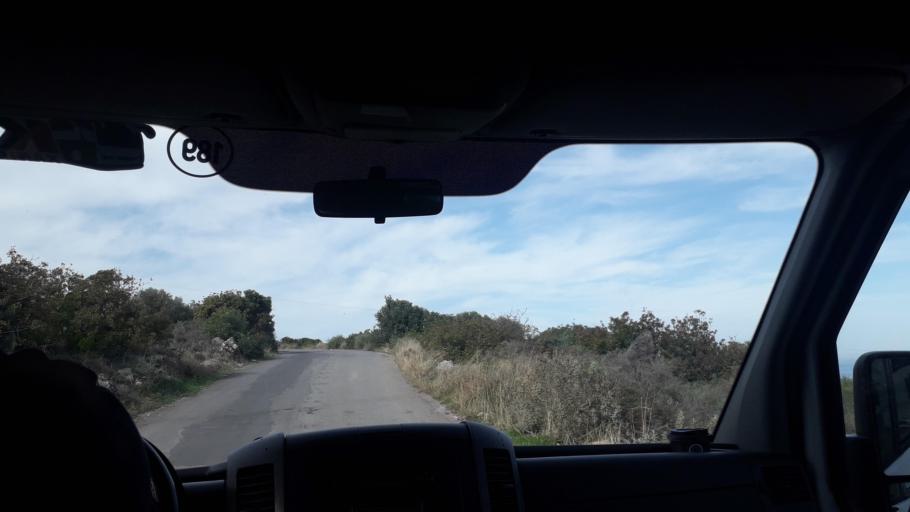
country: GR
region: Crete
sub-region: Nomos Rethymnis
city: Atsipopoulon
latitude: 35.3633
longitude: 24.4355
